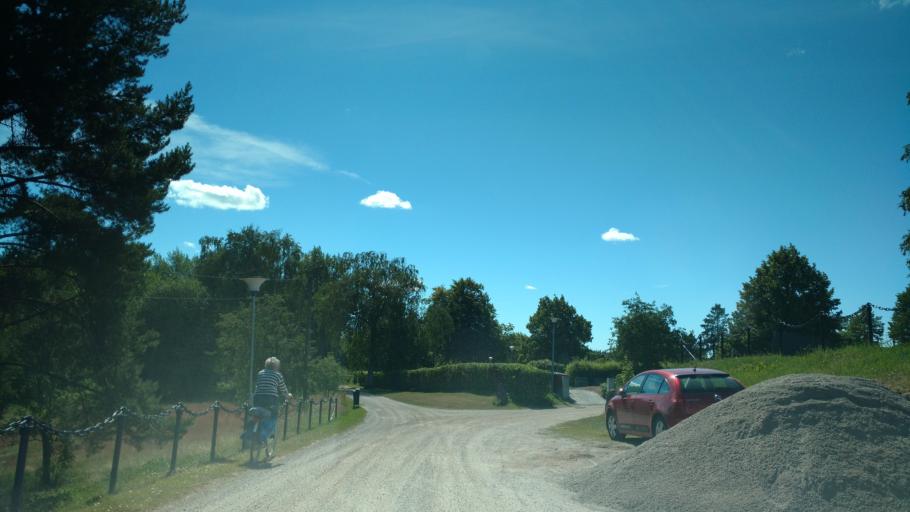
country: FI
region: Varsinais-Suomi
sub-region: Turku
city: Rusko
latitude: 60.5303
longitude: 22.2129
